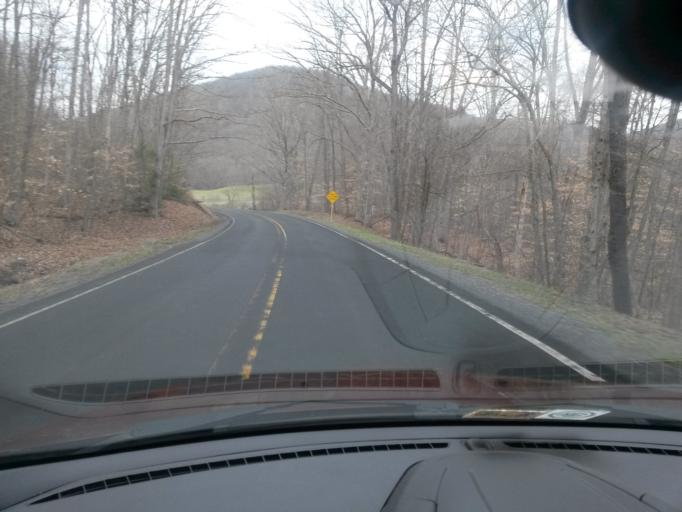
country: US
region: Virginia
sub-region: Bath County
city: Warm Springs
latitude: 38.0695
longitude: -79.7724
